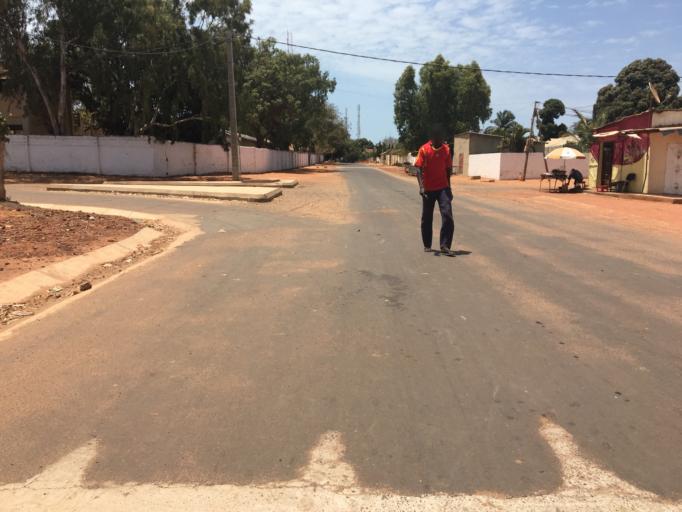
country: GM
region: Banjul
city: Bakau
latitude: 13.4716
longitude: -16.6842
